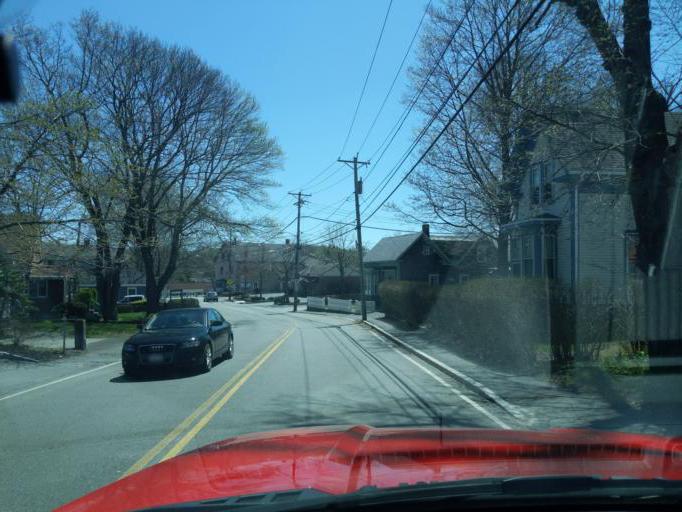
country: US
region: Massachusetts
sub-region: Essex County
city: Rockport
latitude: 42.6572
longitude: -70.6263
